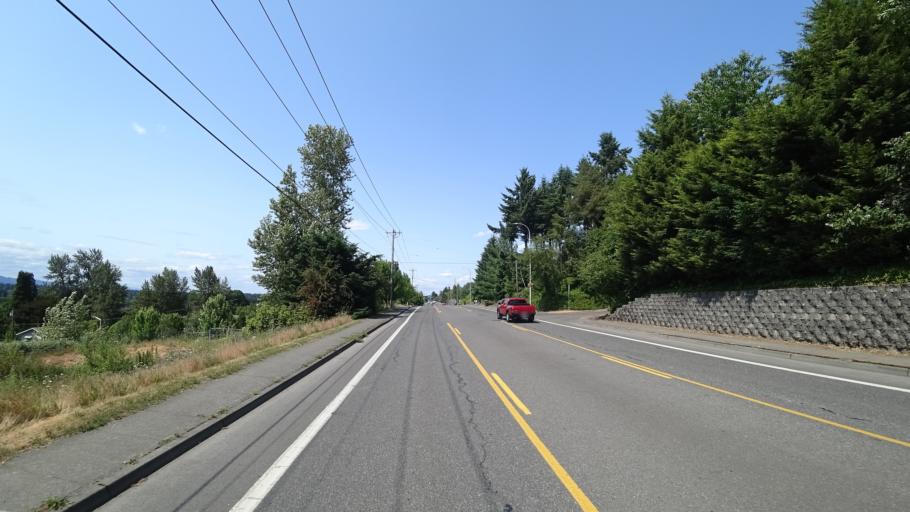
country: US
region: Oregon
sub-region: Multnomah County
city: Lents
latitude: 45.4534
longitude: -122.5688
